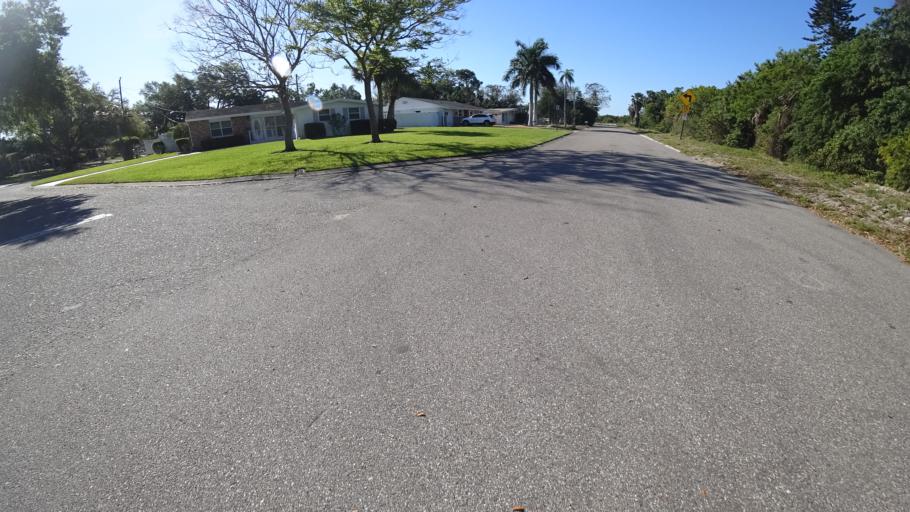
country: US
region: Florida
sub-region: Manatee County
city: Bayshore Gardens
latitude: 27.4246
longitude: -82.5960
